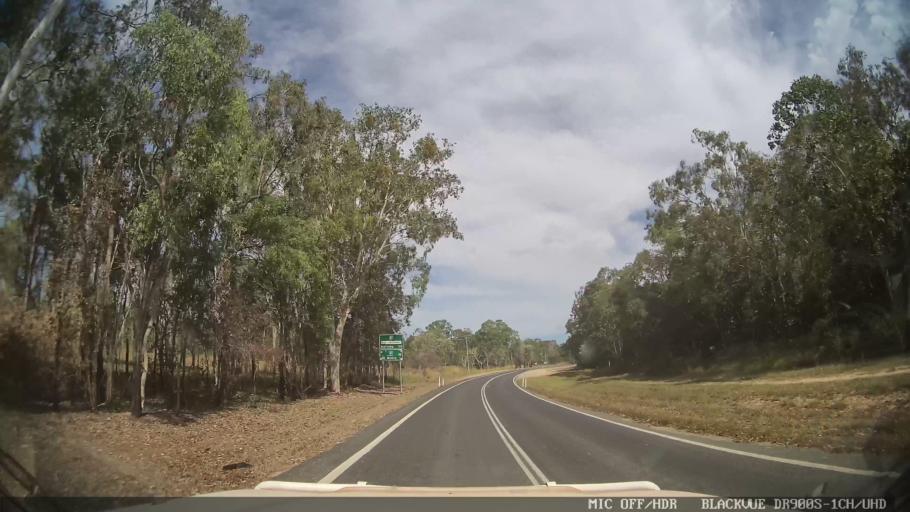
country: AU
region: Queensland
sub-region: Cairns
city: Port Douglas
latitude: -16.6668
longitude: 145.3290
